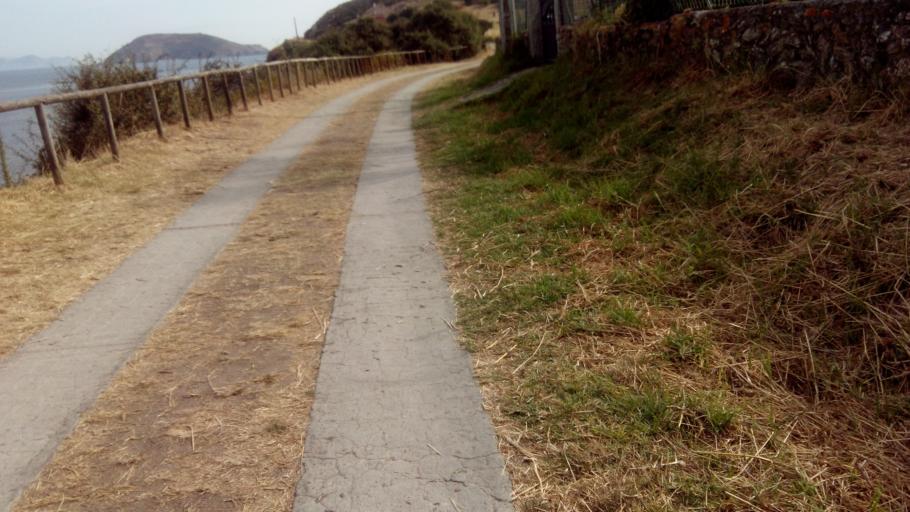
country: ES
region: Galicia
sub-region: Provincia de Pontevedra
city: Sanxenxo
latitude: 42.3699
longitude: -8.9342
